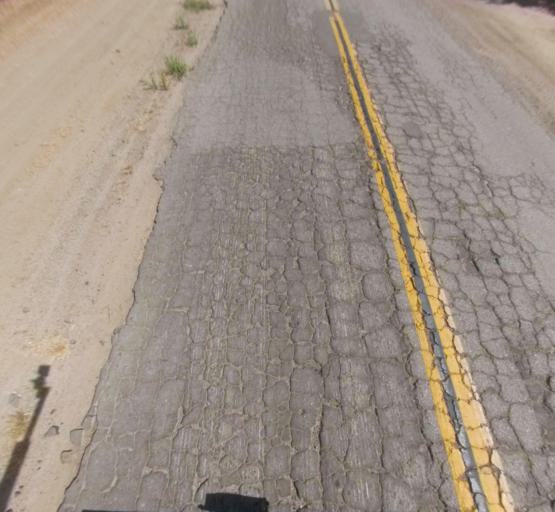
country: US
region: California
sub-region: Madera County
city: Chowchilla
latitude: 37.0912
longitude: -120.4008
